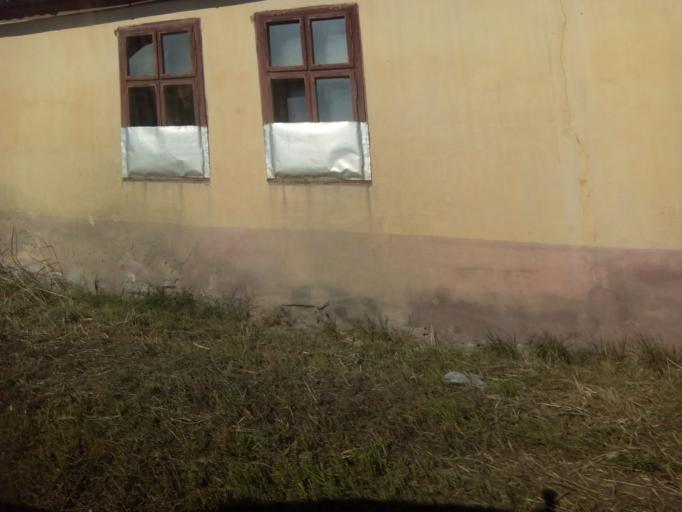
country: RS
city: Celarevo
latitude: 45.2734
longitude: 19.5432
